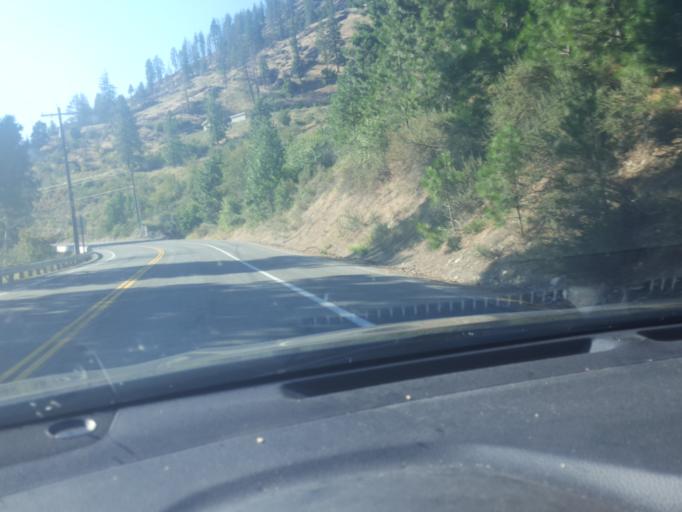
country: US
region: Washington
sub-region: Chelan County
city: Granite Falls
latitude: 47.9901
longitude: -120.2452
